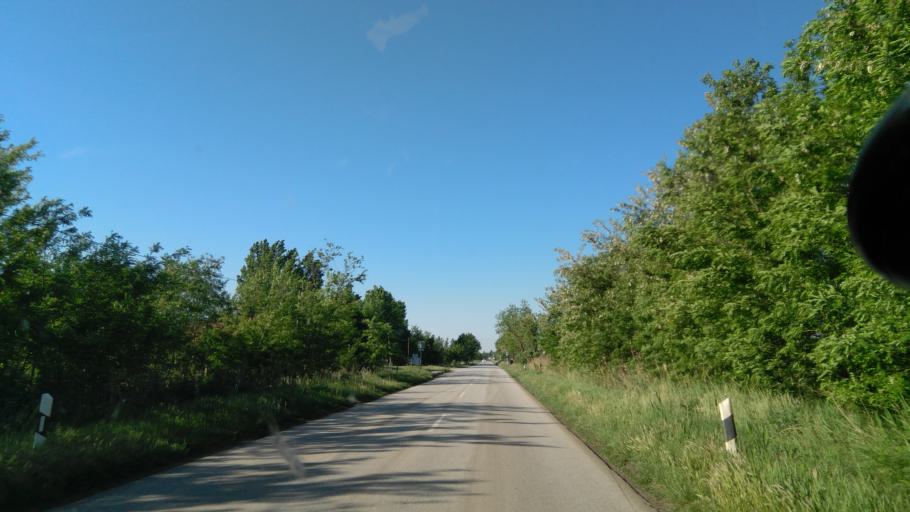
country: HU
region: Bekes
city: Elek
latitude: 46.5440
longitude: 21.2571
